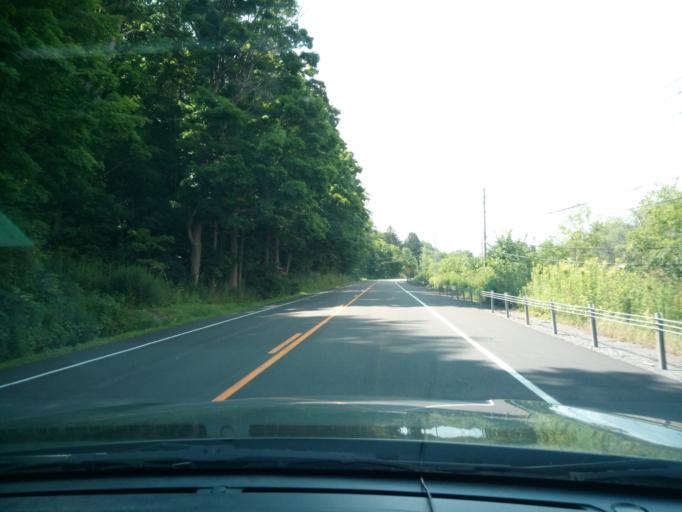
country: US
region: New York
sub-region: Chemung County
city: Southport
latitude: 42.0216
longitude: -76.7386
